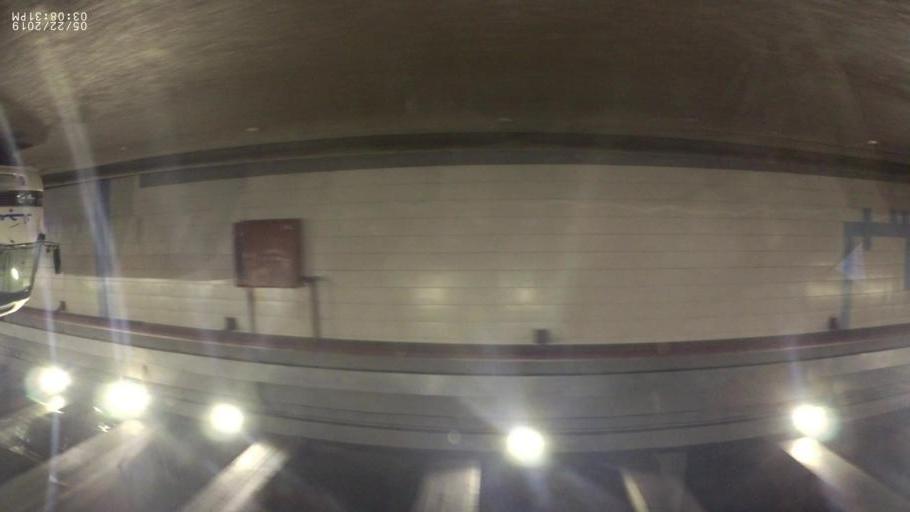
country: LB
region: Beyrouth
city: Beirut
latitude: 33.8843
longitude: 35.4971
